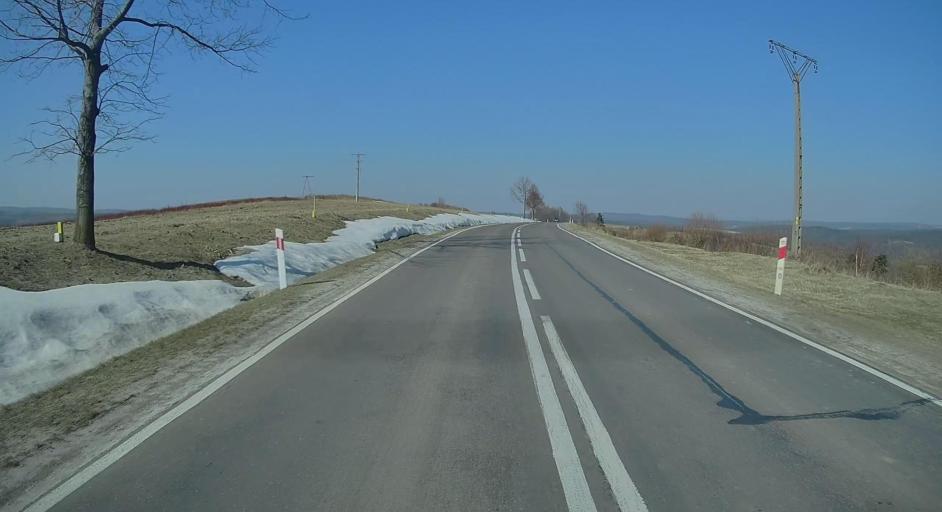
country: PL
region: Subcarpathian Voivodeship
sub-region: Powiat przemyski
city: Bircza
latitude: 49.6367
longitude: 22.4233
